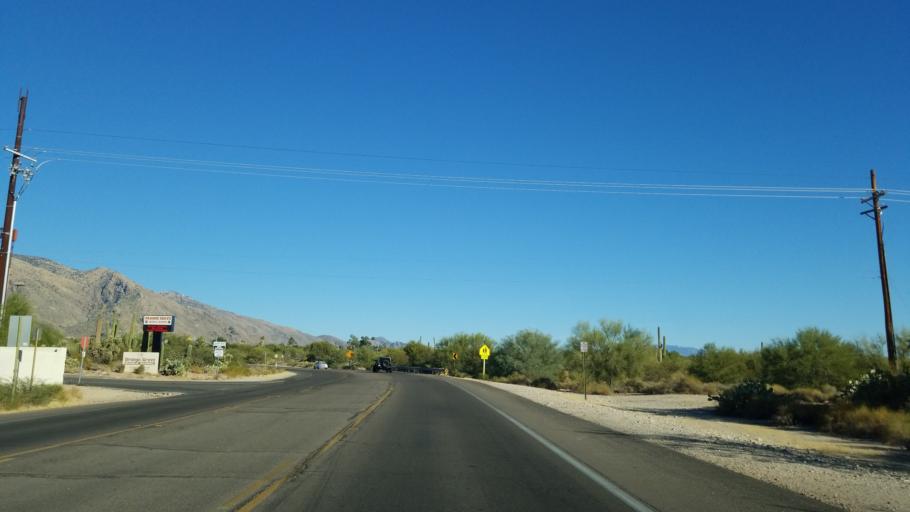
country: US
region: Arizona
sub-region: Pima County
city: Catalina Foothills
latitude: 32.3226
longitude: -110.9445
